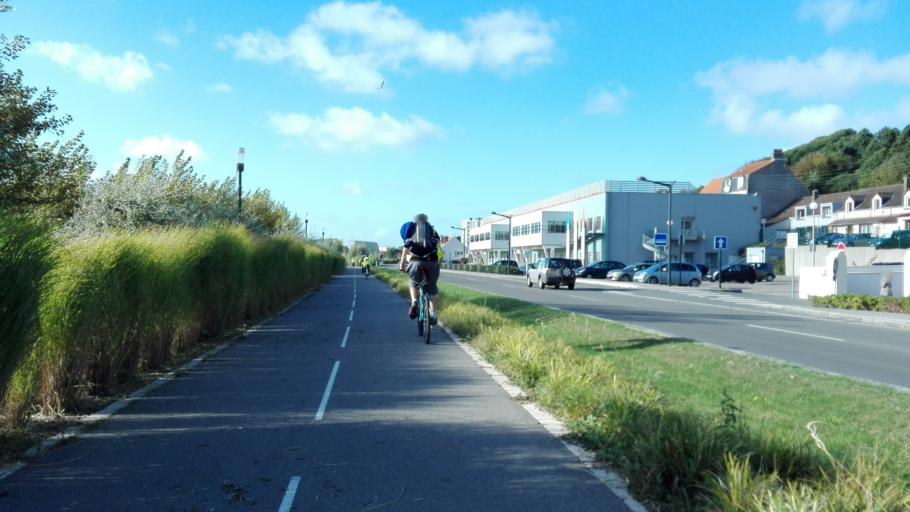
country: FR
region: Nord-Pas-de-Calais
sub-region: Departement du Pas-de-Calais
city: Boulogne-sur-Mer
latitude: 50.7065
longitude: 1.6125
